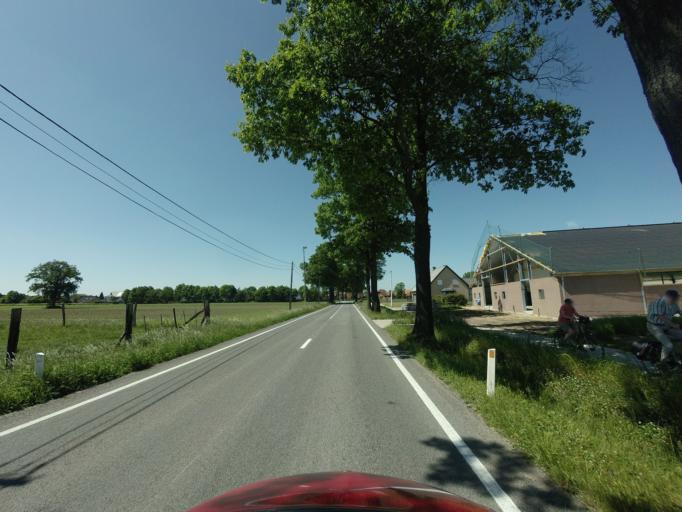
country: BE
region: Flanders
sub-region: Provincie Antwerpen
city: Ravels
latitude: 51.3828
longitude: 5.0198
